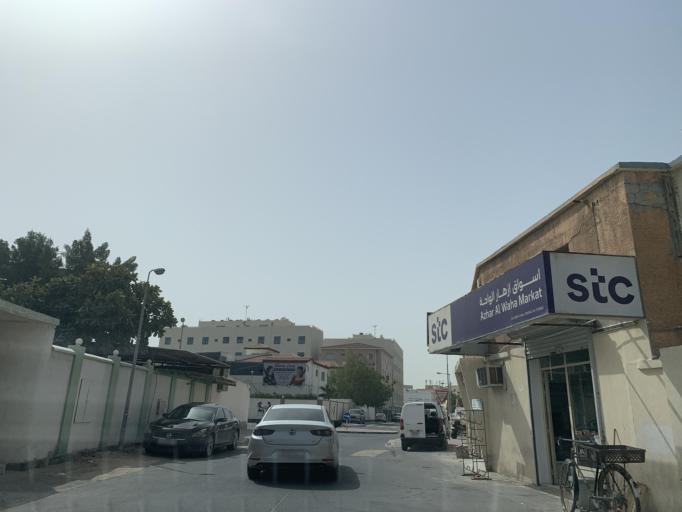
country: BH
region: Manama
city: Manama
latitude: 26.2085
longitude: 50.6005
